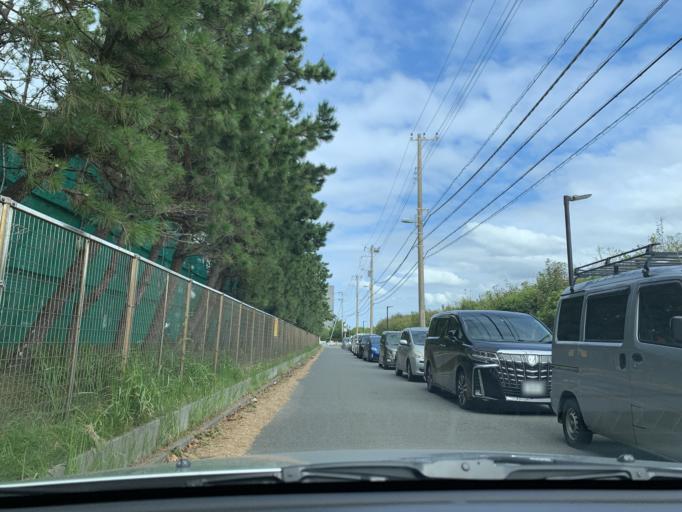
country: JP
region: Tokyo
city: Urayasu
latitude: 35.6184
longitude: 139.8998
